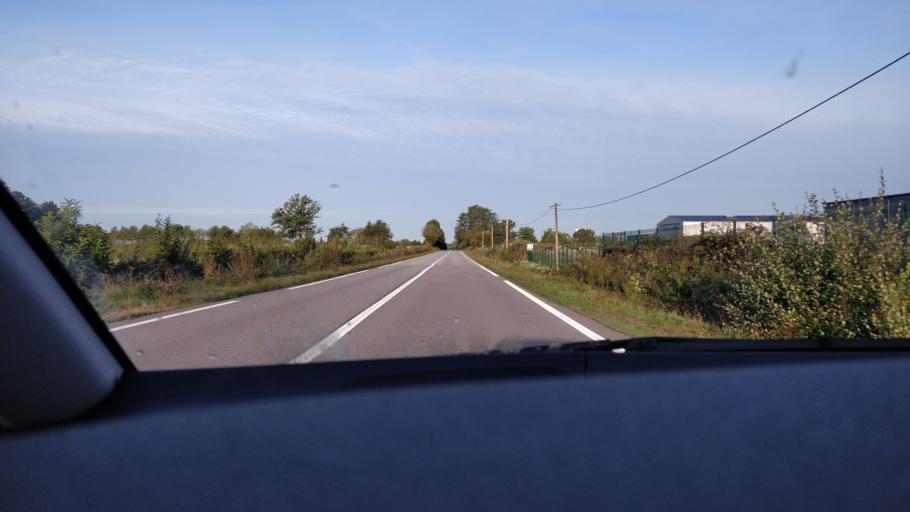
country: FR
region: Limousin
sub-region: Departement de la Haute-Vienne
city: Saint-Just-le-Martel
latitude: 45.8469
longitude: 1.3678
